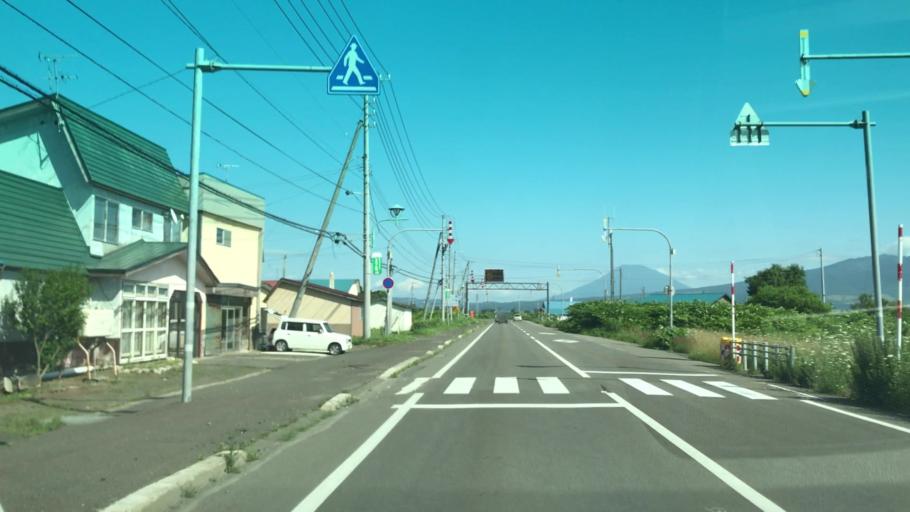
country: JP
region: Hokkaido
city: Iwanai
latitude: 43.0308
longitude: 140.5377
